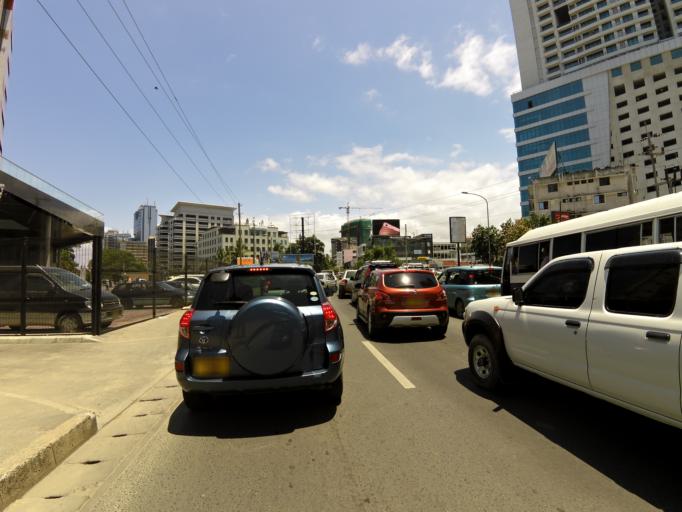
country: TZ
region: Dar es Salaam
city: Dar es Salaam
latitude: -6.8097
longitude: 39.2868
